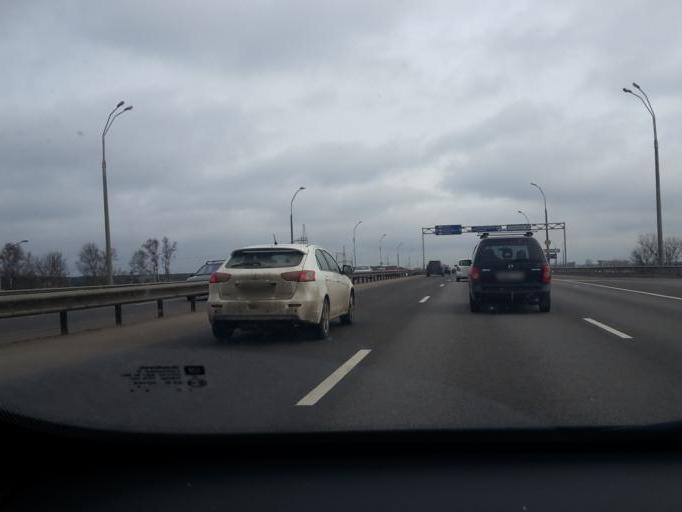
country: BY
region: Minsk
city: Zhdanovichy
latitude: 53.9413
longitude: 27.4331
